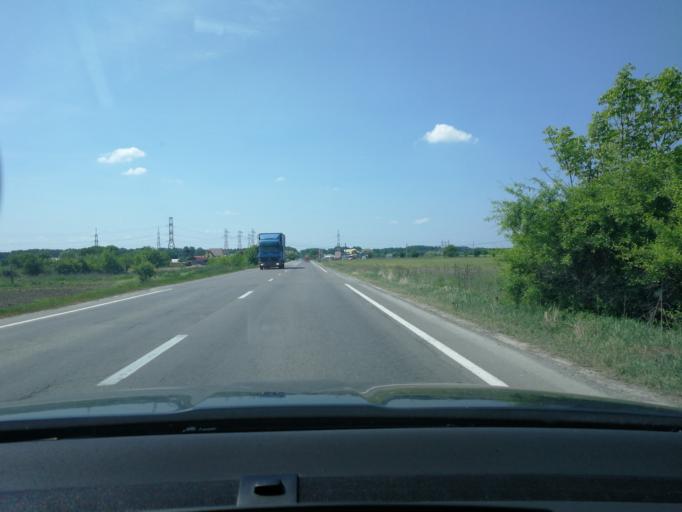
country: RO
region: Prahova
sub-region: Comuna Targsoru Vechi
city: Targsoru Vechi
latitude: 44.8648
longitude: 25.9295
